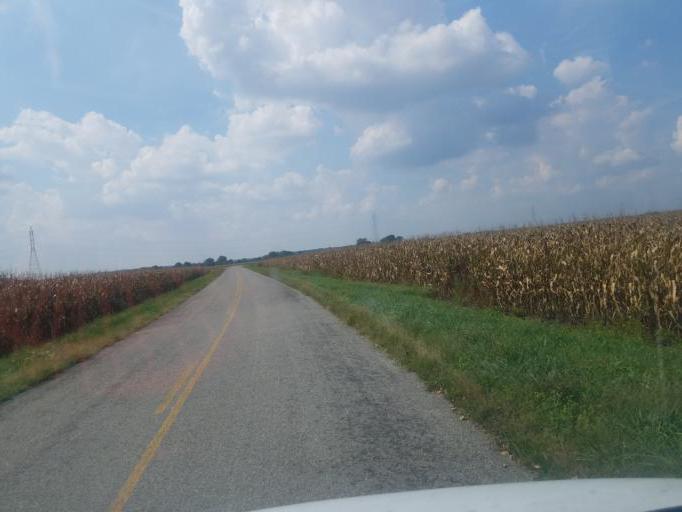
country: US
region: Ohio
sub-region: Hardin County
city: Ada
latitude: 40.6383
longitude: -83.7947
